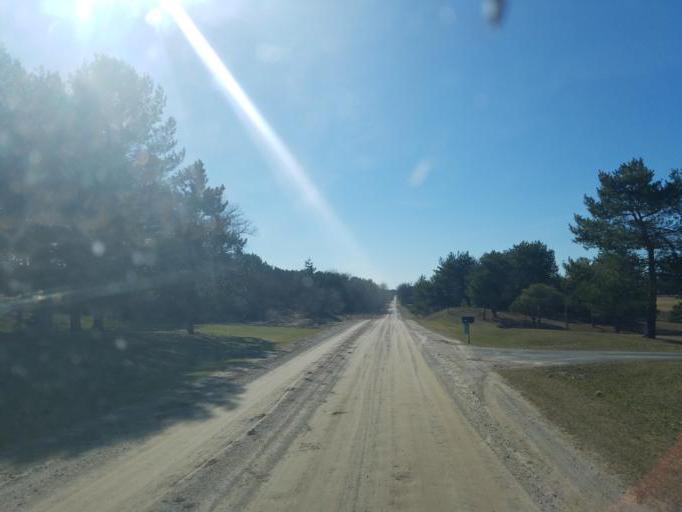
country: US
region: Michigan
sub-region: Isabella County
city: Lake Isabella
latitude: 43.5526
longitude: -85.0594
